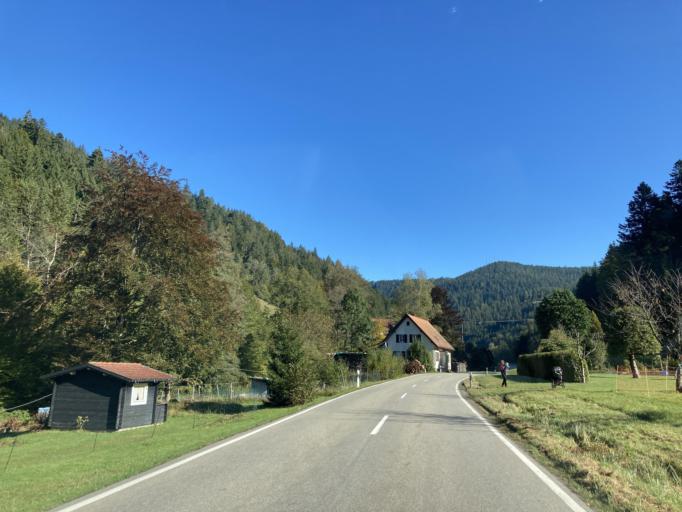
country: DE
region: Baden-Wuerttemberg
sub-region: Karlsruhe Region
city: Bad Rippoldsau-Schapbach
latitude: 48.4082
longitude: 8.3203
